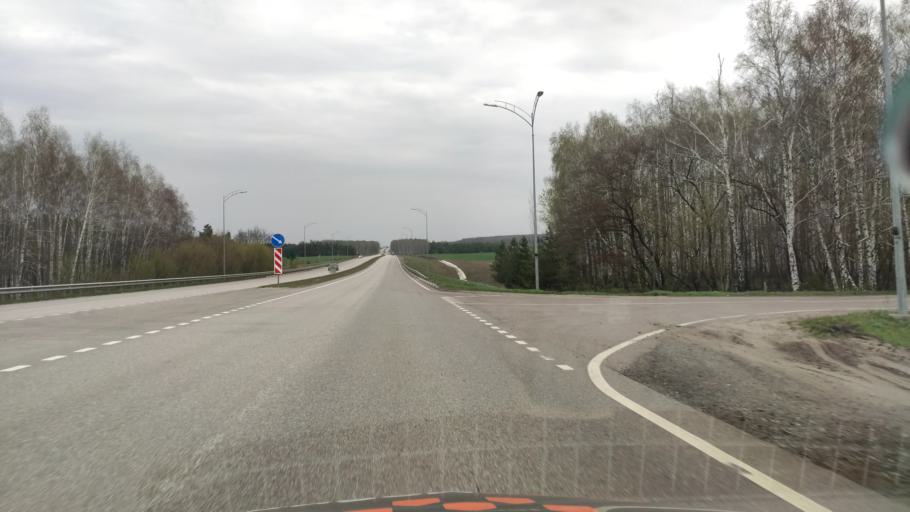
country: RU
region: Belgorod
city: Staryy Oskol
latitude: 51.4013
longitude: 37.8762
